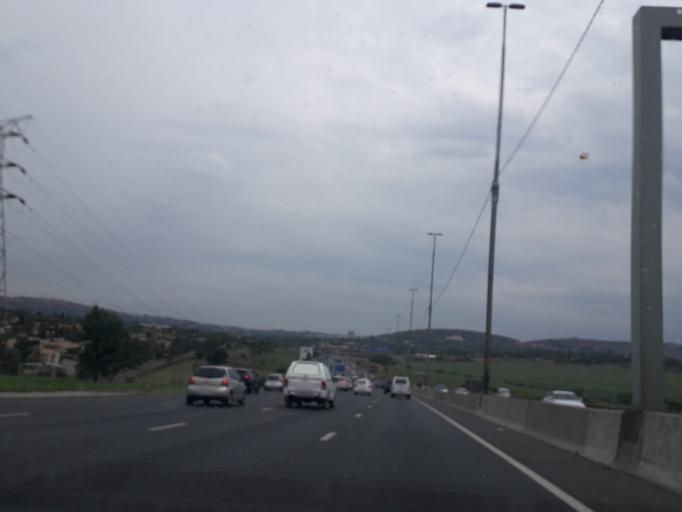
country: ZA
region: Gauteng
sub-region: City of Johannesburg Metropolitan Municipality
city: Modderfontein
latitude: -26.1327
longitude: 28.1337
